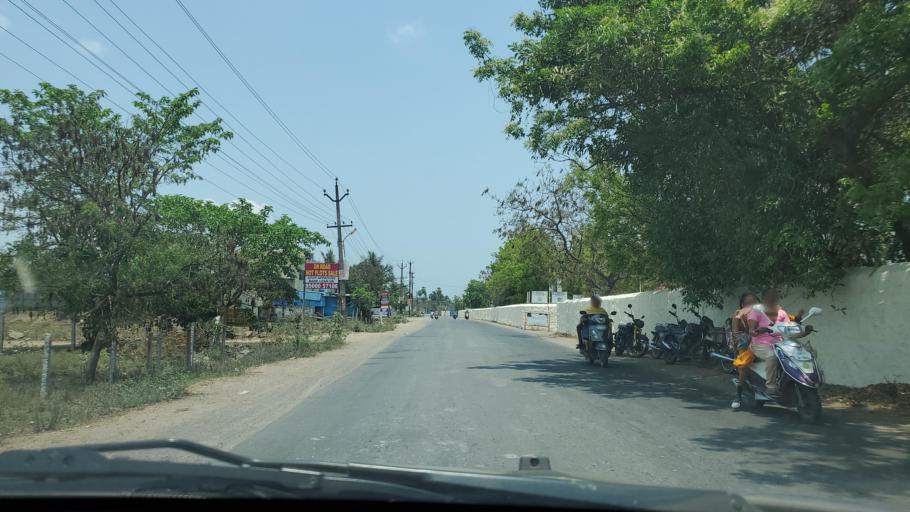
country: IN
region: Tamil Nadu
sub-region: Kancheepuram
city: Vengavasal
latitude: 12.8505
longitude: 80.1708
